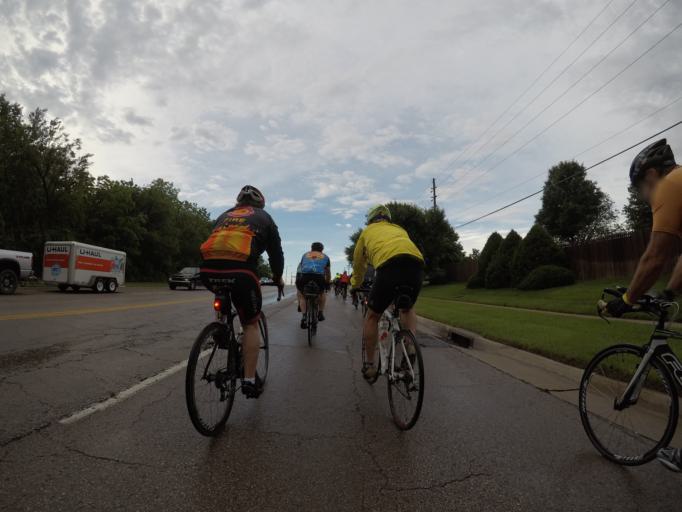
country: US
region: Kansas
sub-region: Shawnee County
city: Topeka
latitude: 39.0022
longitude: -95.7060
